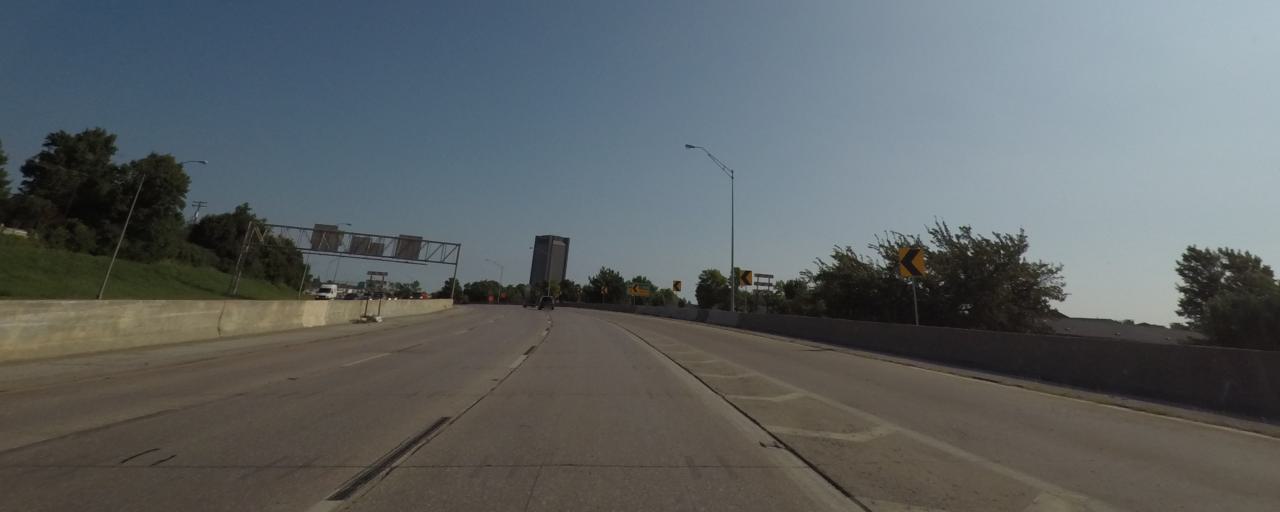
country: US
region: Oklahoma
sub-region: Oklahoma County
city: Nichols Hills
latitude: 35.5155
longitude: -97.5451
